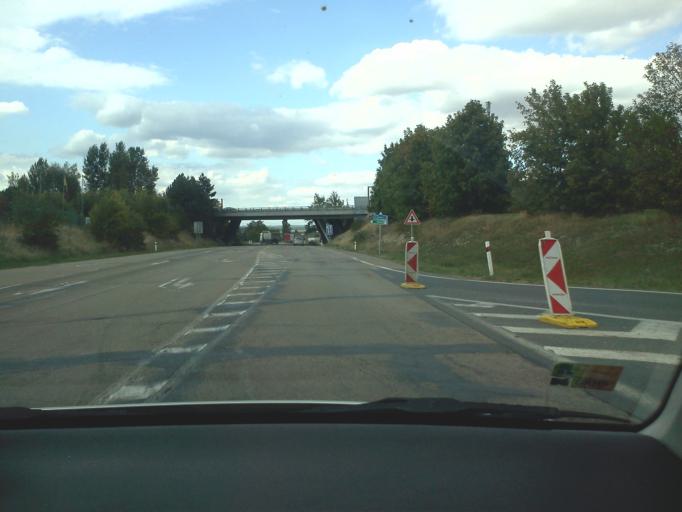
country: CZ
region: Central Bohemia
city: Prerov nad Labem
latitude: 50.1355
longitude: 14.8455
